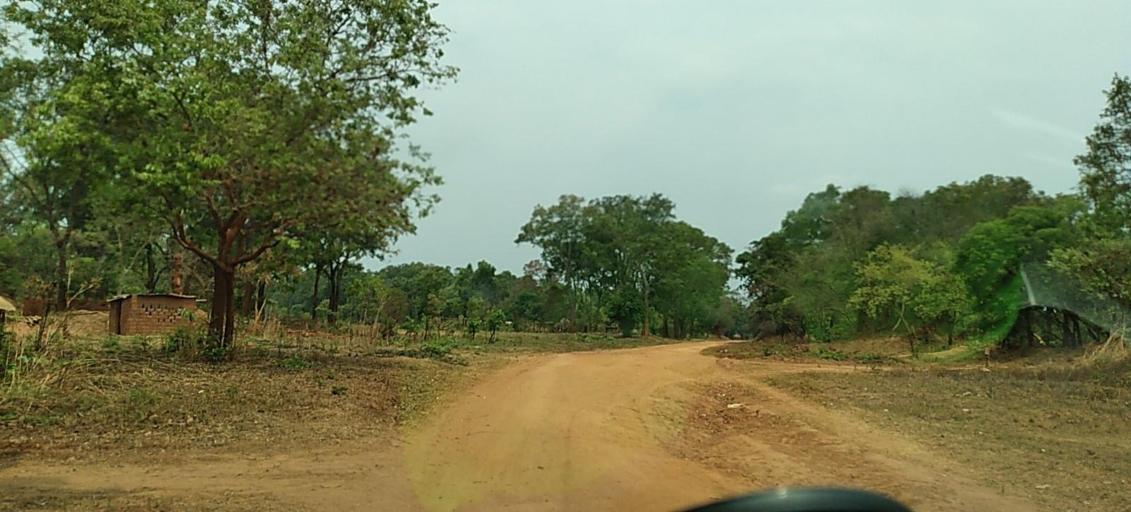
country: ZM
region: North-Western
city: Solwezi
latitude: -12.8029
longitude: 26.5369
